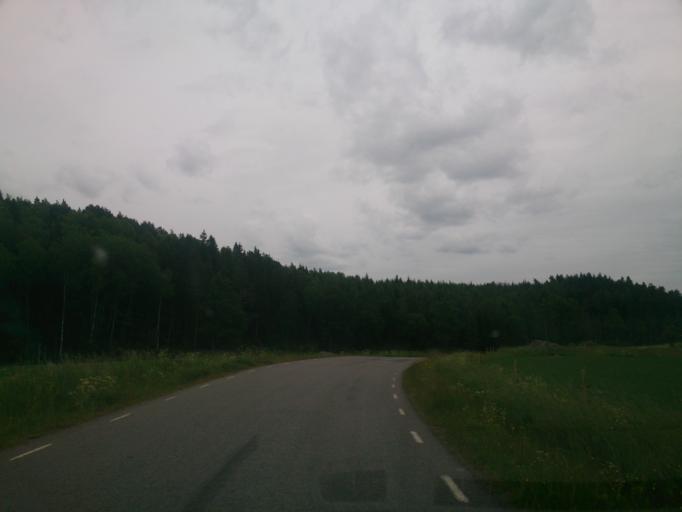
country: SE
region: OEstergoetland
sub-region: Atvidabergs Kommun
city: Atvidaberg
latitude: 58.3228
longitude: 16.0502
